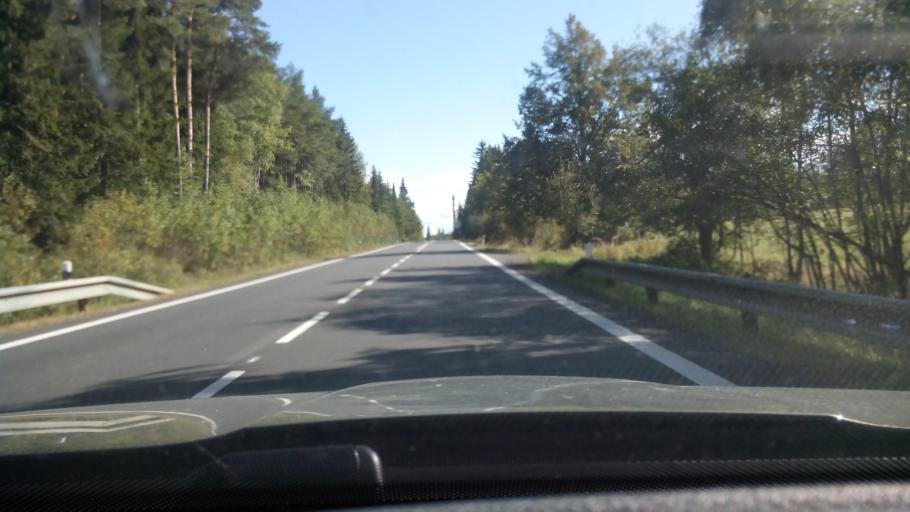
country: CZ
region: Jihocesky
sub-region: Okres Prachatice
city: Zdikov
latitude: 49.0658
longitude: 13.7301
